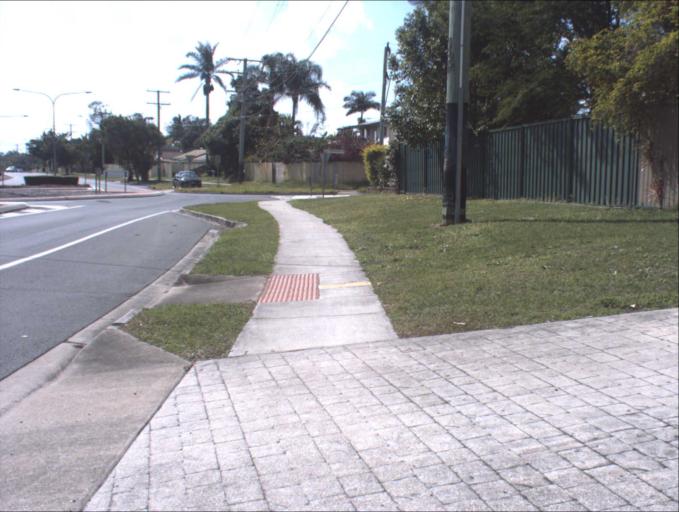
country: AU
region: Queensland
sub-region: Logan
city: Park Ridge South
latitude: -27.6963
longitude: 153.0131
